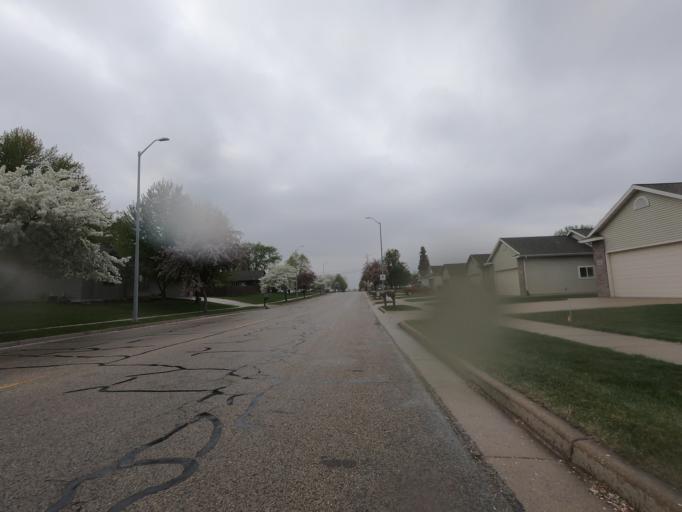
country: US
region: Wisconsin
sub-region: Jefferson County
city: Jefferson
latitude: 43.0123
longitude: -88.8154
